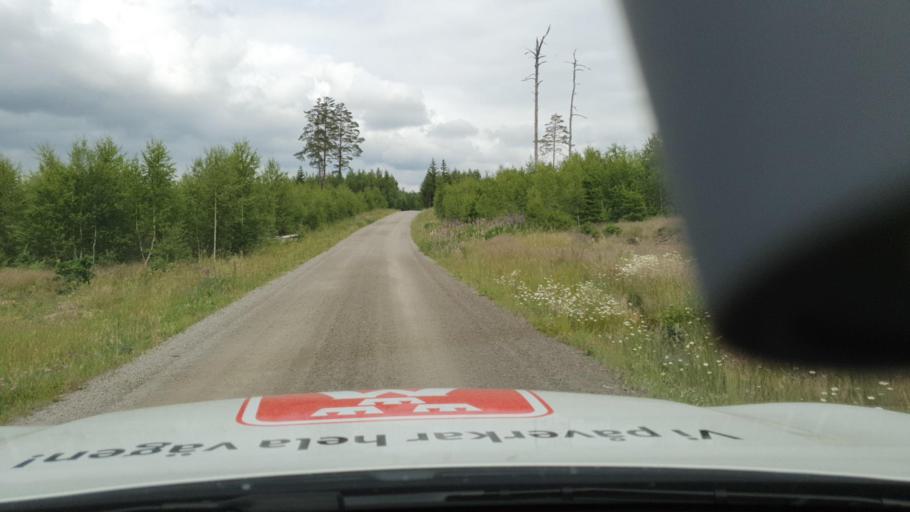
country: SE
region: Vaestra Goetaland
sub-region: Tidaholms Kommun
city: Tidaholm
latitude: 58.1527
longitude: 14.0298
